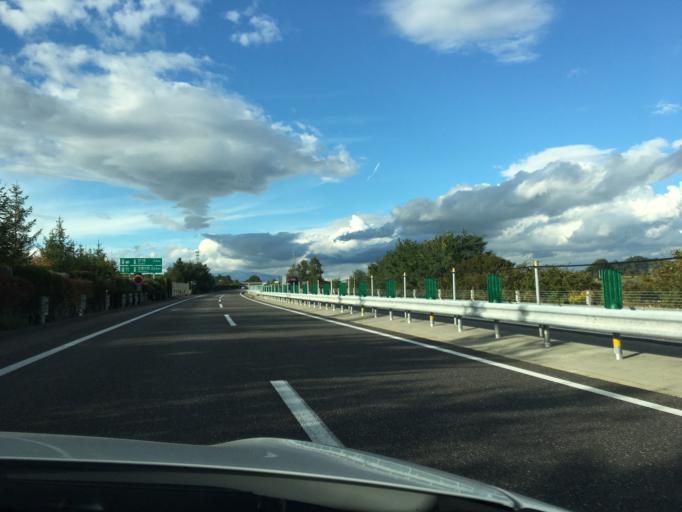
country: JP
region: Fukushima
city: Sukagawa
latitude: 37.3291
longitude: 140.3379
